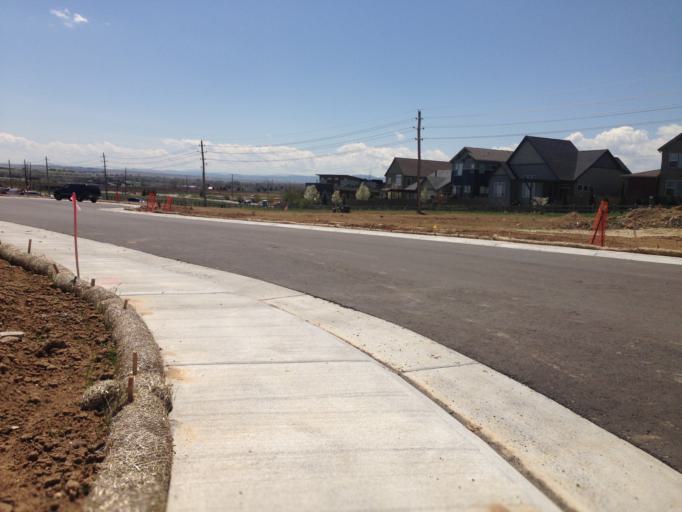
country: US
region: Colorado
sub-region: Boulder County
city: Louisville
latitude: 39.9899
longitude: -105.1180
